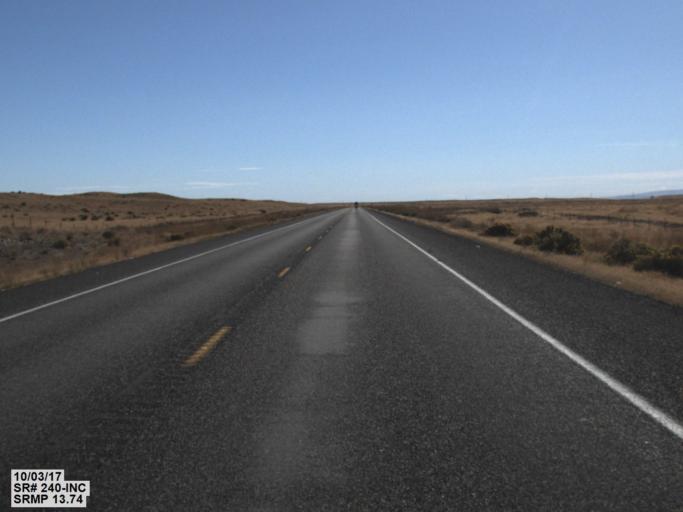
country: US
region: Washington
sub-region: Benton County
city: Benton City
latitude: 46.4552
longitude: -119.5162
